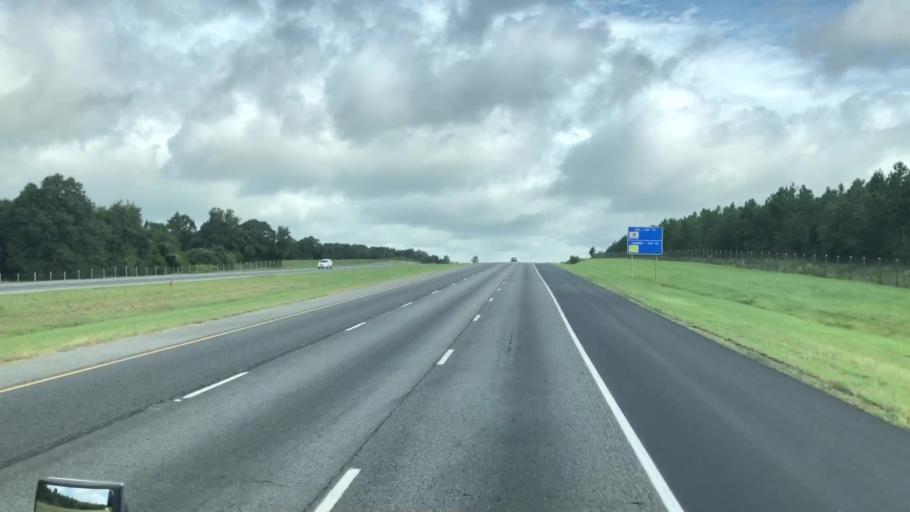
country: US
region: Georgia
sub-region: Turner County
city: Ashburn
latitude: 31.8132
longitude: -83.7079
